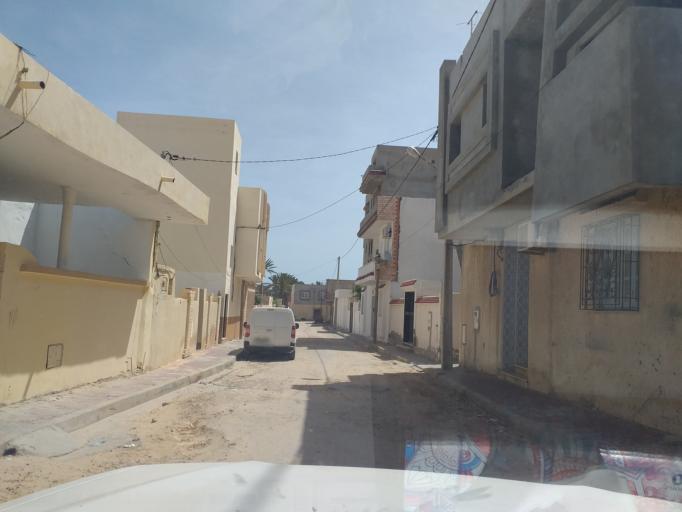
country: TN
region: Qabis
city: Gabes
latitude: 33.9416
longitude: 10.0694
